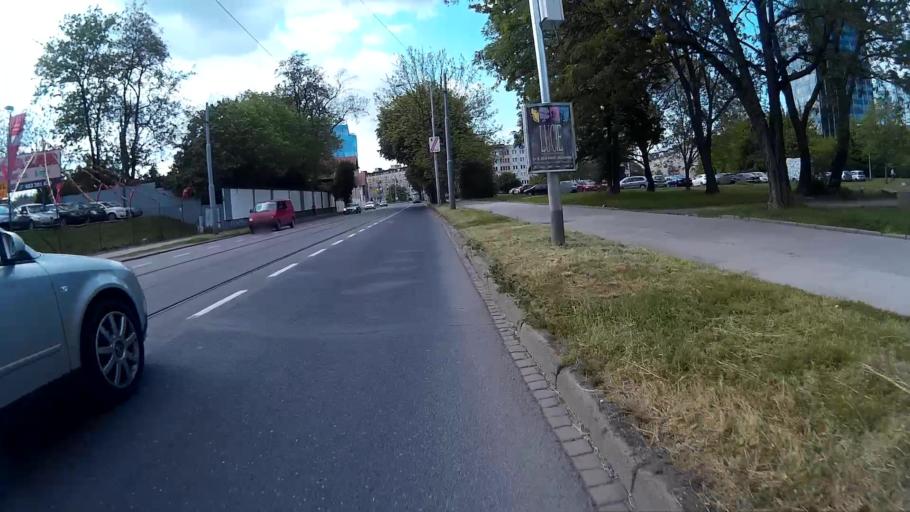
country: CZ
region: South Moravian
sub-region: Mesto Brno
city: Brno
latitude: 49.2083
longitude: 16.5910
